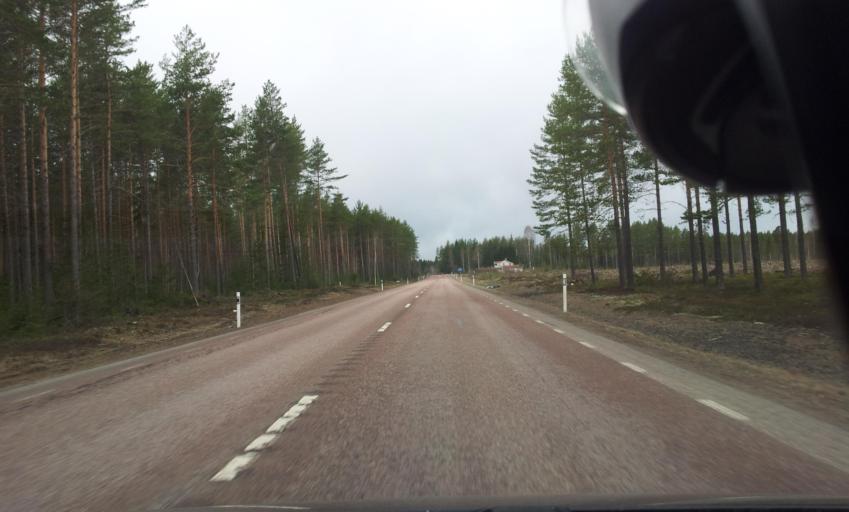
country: SE
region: Gaevleborg
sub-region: Ljusdals Kommun
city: Ljusdal
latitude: 61.8148
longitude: 15.9738
